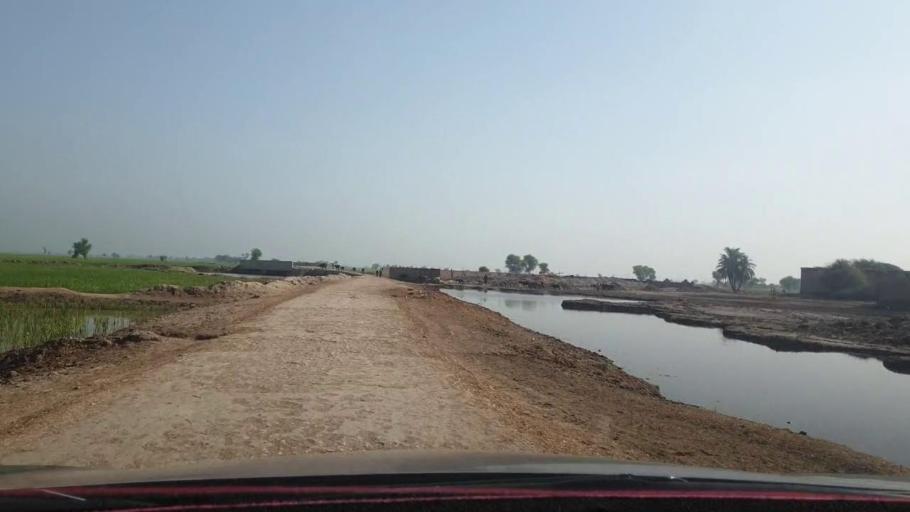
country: PK
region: Sindh
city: Nasirabad
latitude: 27.4636
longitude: 67.9195
